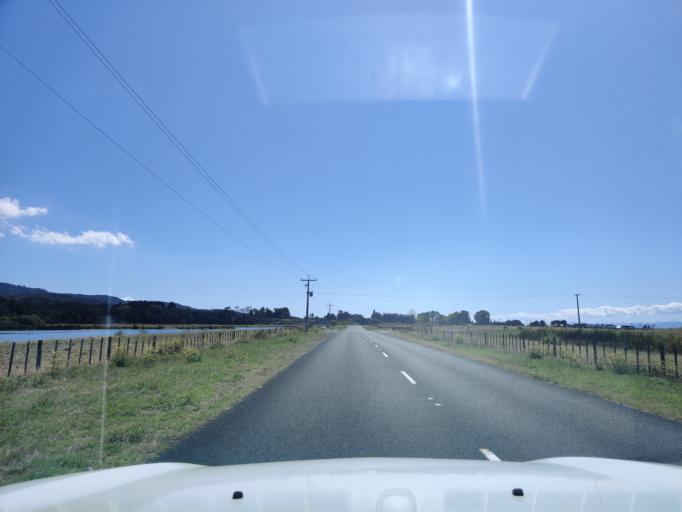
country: NZ
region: Waikato
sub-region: Thames-Coromandel District
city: Thames
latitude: -37.0627
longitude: 175.2983
